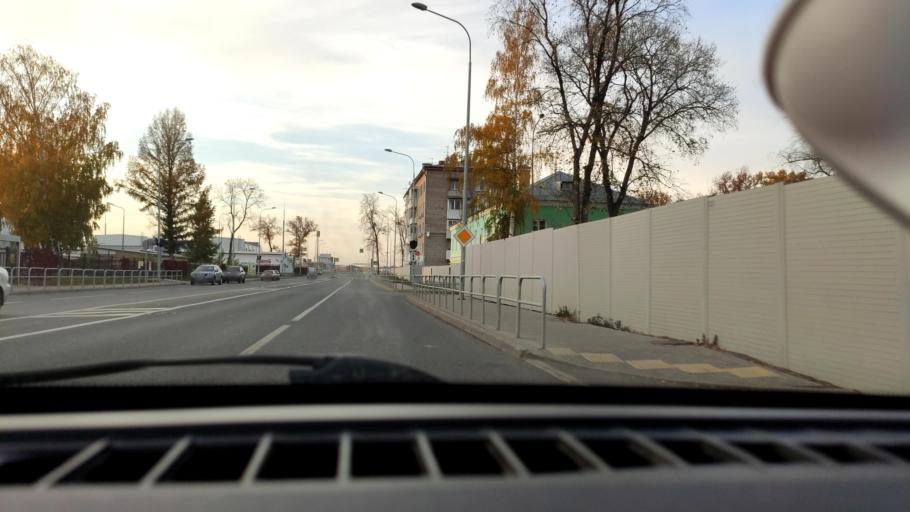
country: RU
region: Samara
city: Samara
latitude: 53.2665
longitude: 50.2410
